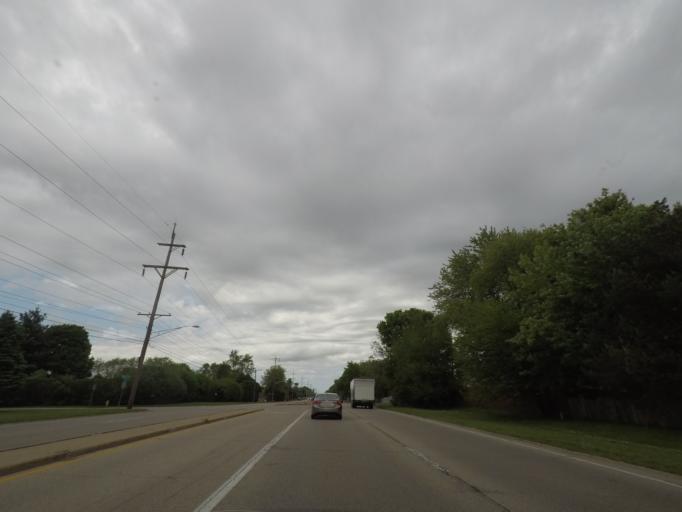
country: US
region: Illinois
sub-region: Winnebago County
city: Loves Park
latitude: 42.3019
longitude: -89.0290
